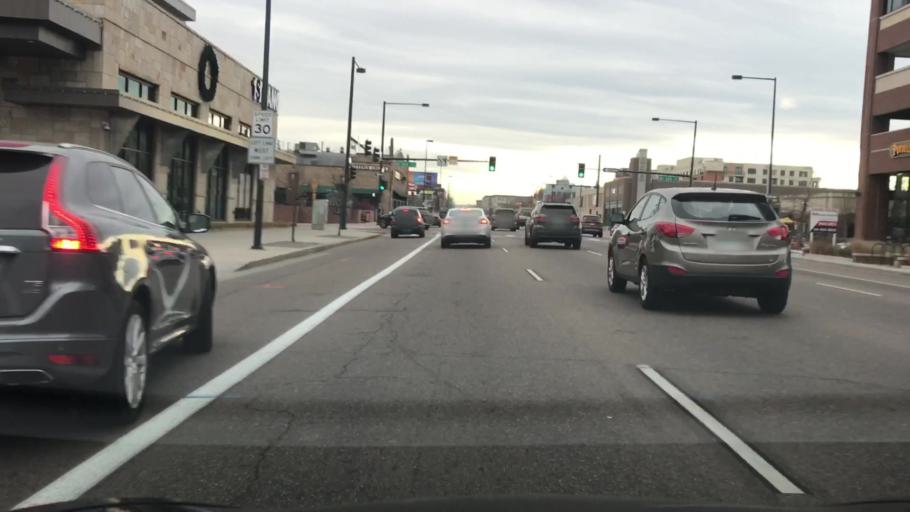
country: US
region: Colorado
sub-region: Denver County
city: Denver
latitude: 39.7262
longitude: -104.9874
